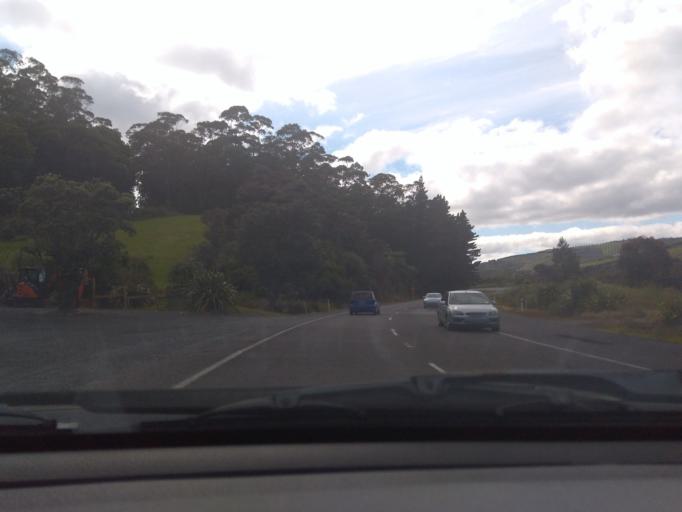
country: NZ
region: Northland
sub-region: Far North District
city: Taipa
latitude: -35.0111
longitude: 173.5509
